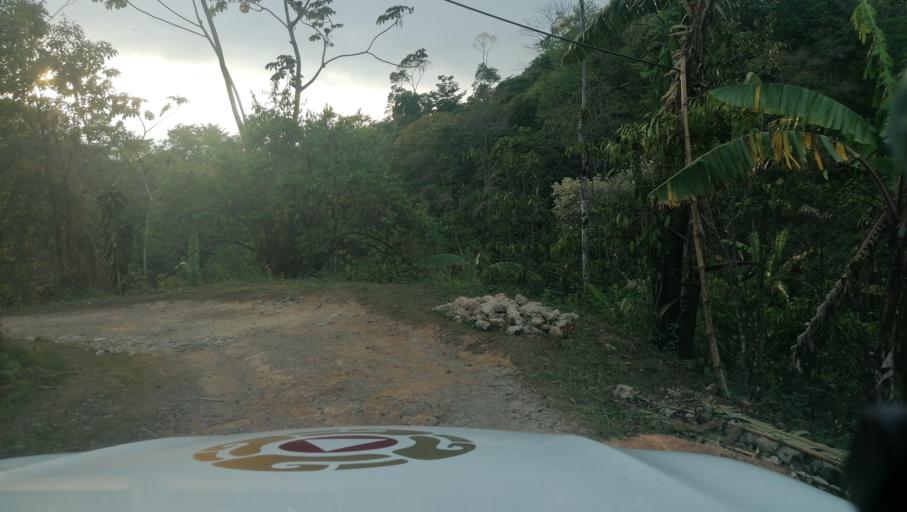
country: MX
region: Chiapas
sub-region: Cacahoatan
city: Benito Juarez
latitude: 15.1001
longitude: -92.2207
